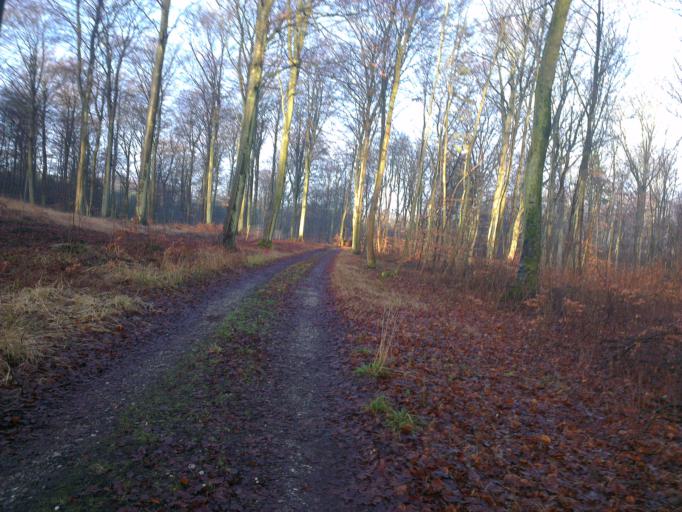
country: DK
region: Capital Region
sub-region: Frederikssund Kommune
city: Jaegerspris
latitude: 55.8843
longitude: 11.9940
